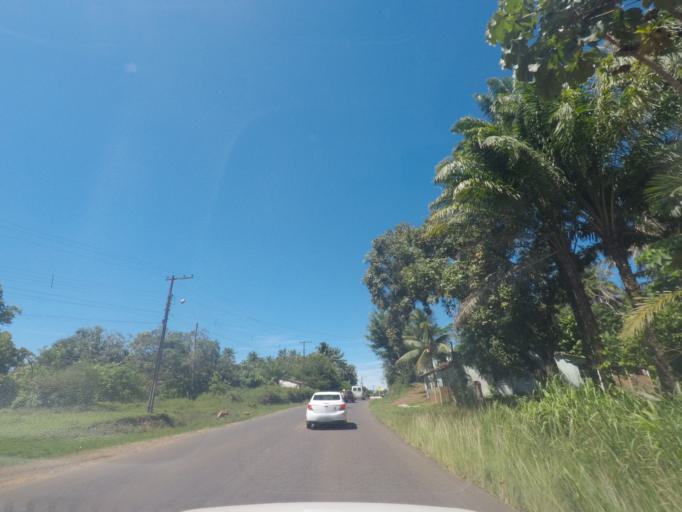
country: BR
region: Bahia
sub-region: Taperoa
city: Taperoa
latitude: -13.4601
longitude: -39.0892
